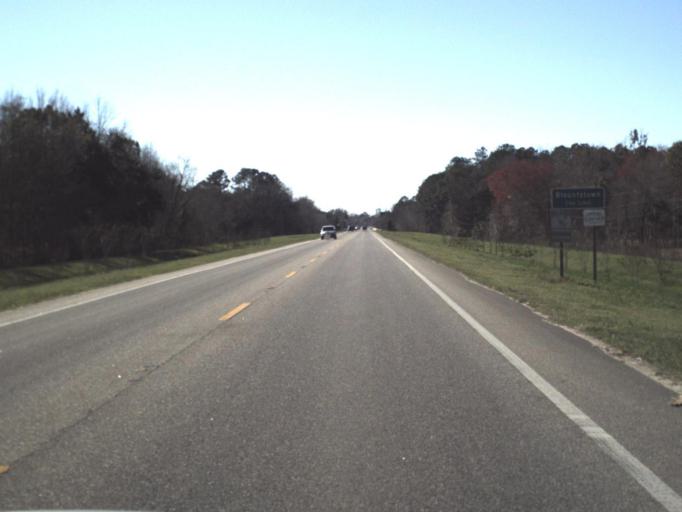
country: US
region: Florida
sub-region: Calhoun County
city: Blountstown
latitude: 30.4432
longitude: -85.0328
